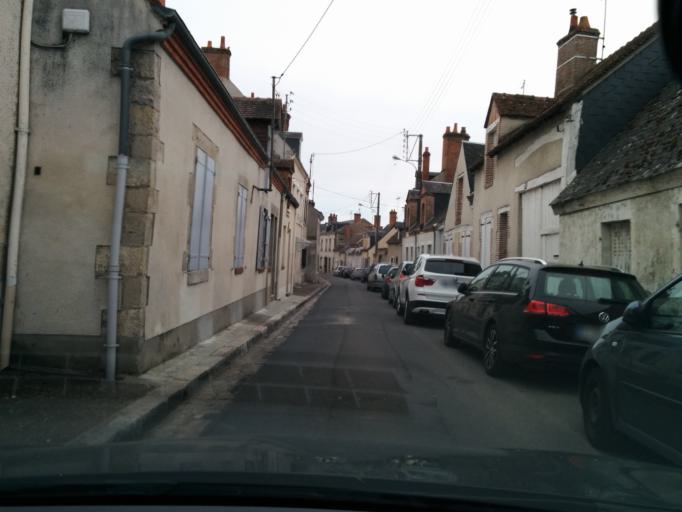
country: FR
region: Centre
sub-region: Departement du Loiret
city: Chateauneuf-sur-Loire
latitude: 47.8613
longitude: 2.2215
